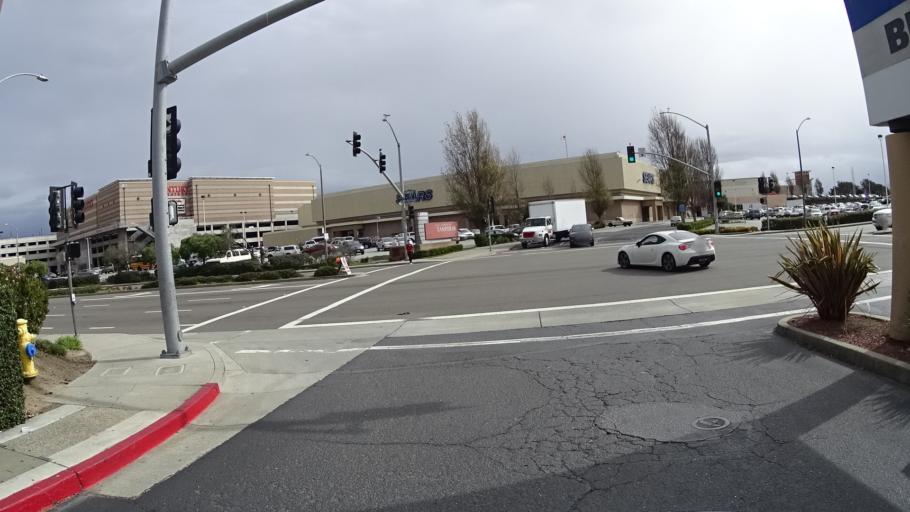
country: US
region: California
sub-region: San Mateo County
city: San Bruno
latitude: 37.6380
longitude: -122.4201
